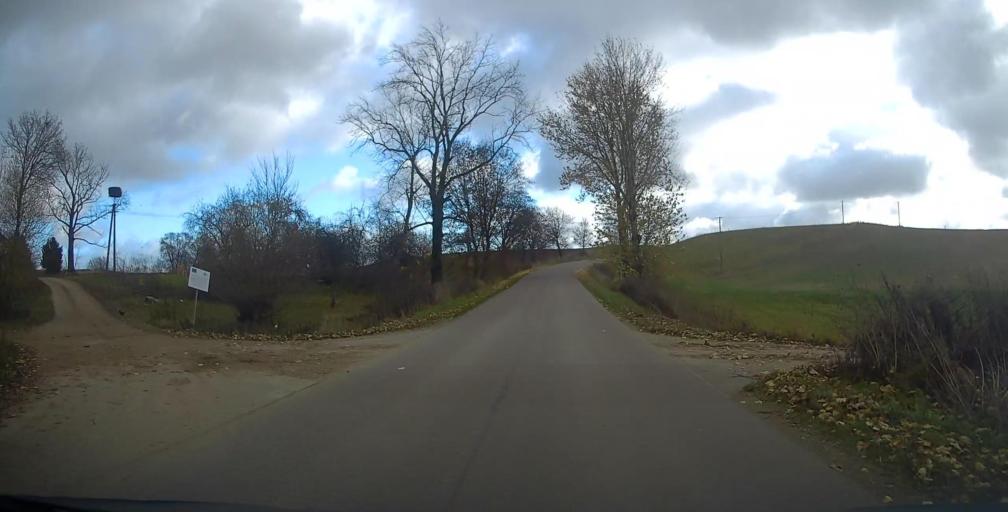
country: PL
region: Podlasie
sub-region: Suwalki
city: Suwalki
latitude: 54.3426
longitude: 22.8586
